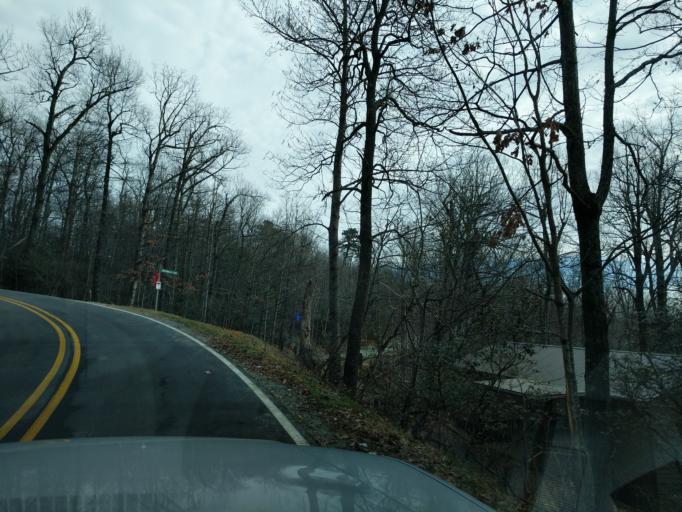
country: US
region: North Carolina
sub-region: Polk County
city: Columbus
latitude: 35.2754
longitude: -82.2265
